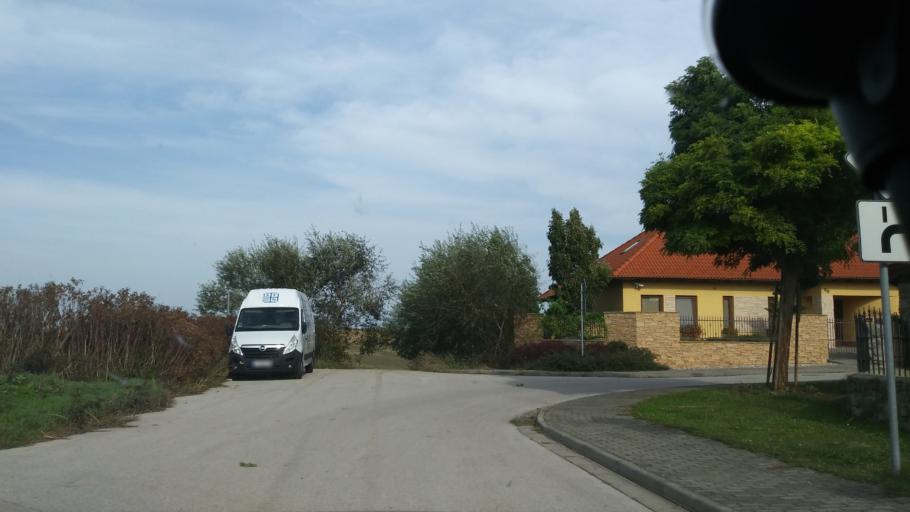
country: SK
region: Trnavsky
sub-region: Okres Skalica
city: Skalica
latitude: 48.8494
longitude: 17.2419
